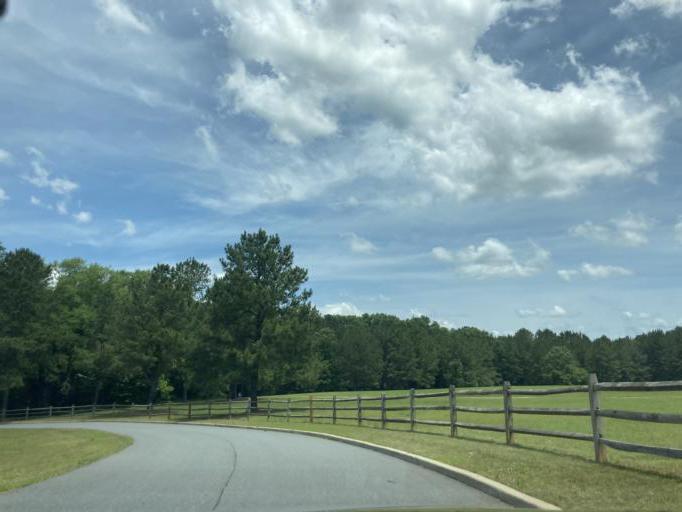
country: US
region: Georgia
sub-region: Bibb County
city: Macon
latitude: 32.8758
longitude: -83.6537
